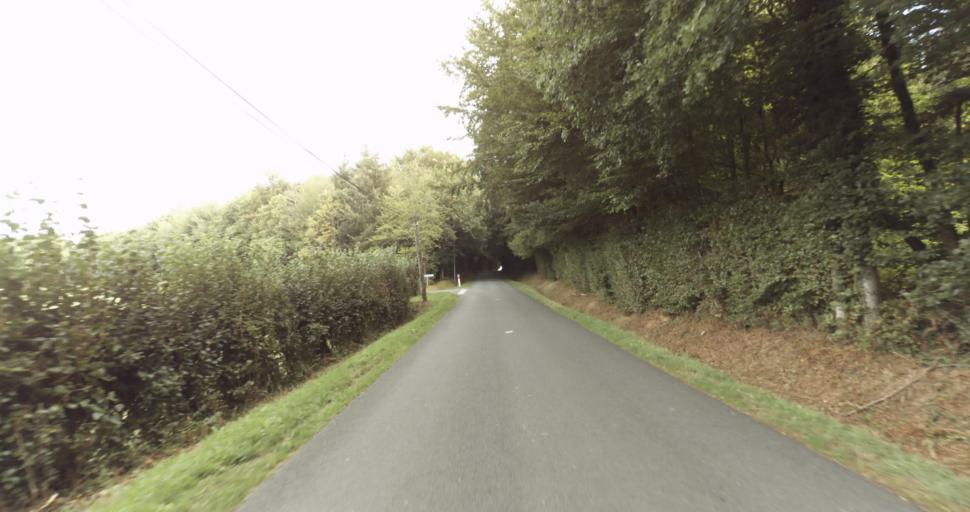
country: FR
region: Lower Normandy
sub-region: Departement de l'Orne
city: Gace
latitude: 48.8210
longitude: 0.2342
